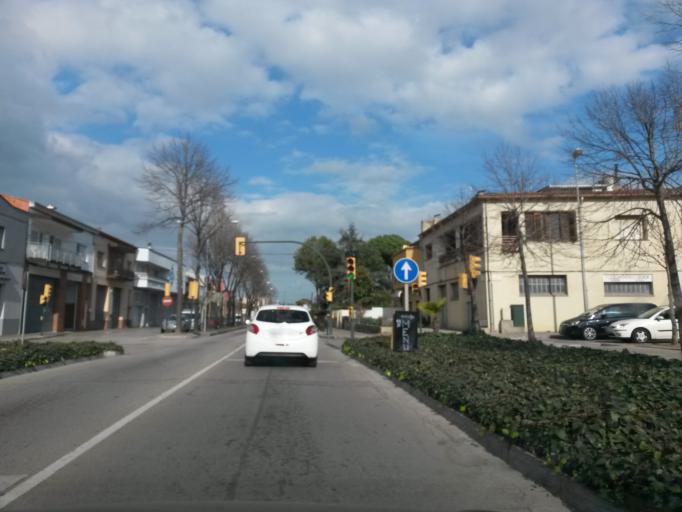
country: ES
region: Catalonia
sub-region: Provincia de Girona
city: Sarria de Ter
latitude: 42.0070
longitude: 2.8250
